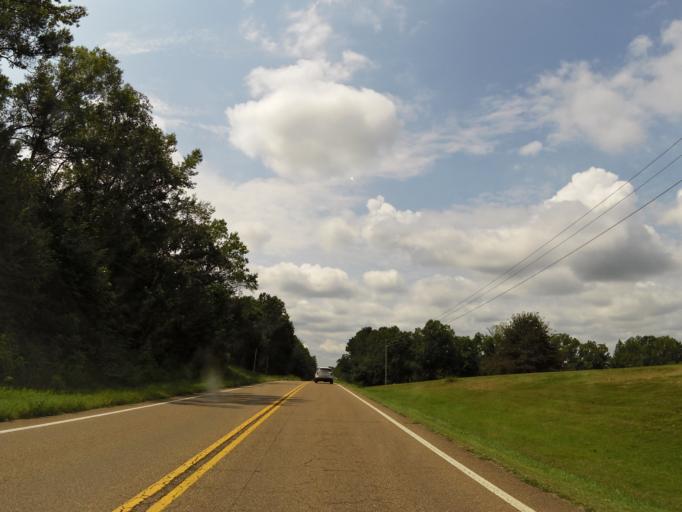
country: US
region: Tennessee
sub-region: Decatur County
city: Decaturville
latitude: 35.5330
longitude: -88.2326
